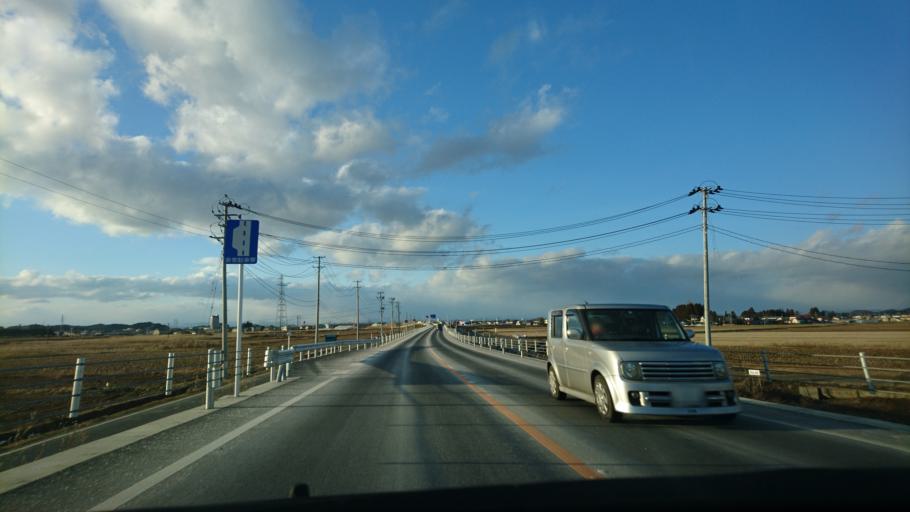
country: JP
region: Miyagi
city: Wakuya
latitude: 38.6902
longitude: 141.2198
